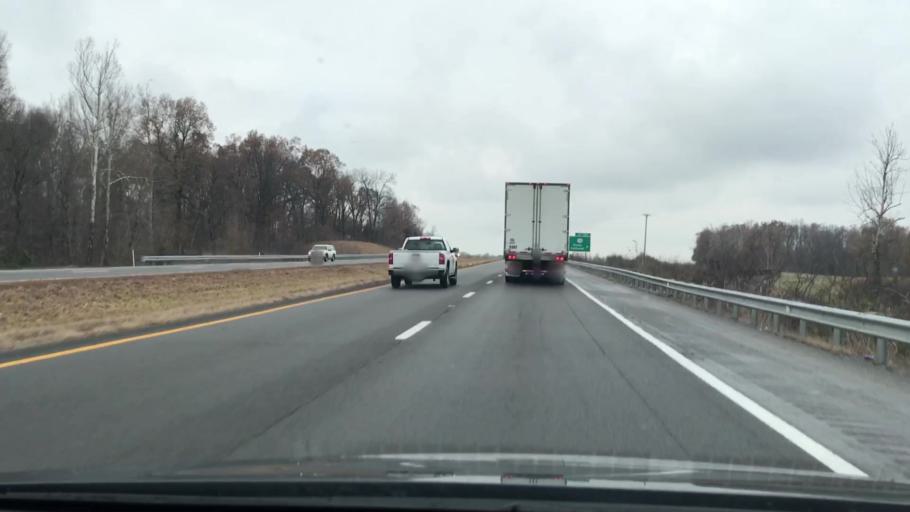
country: US
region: Kentucky
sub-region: Webster County
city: Sebree
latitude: 37.4823
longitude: -87.4756
